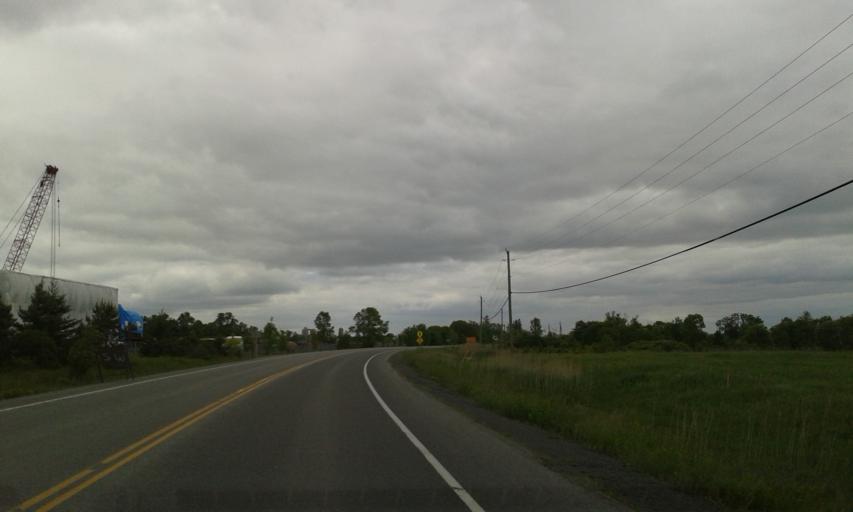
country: CA
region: Ontario
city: Skatepark
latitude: 44.1508
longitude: -76.8365
